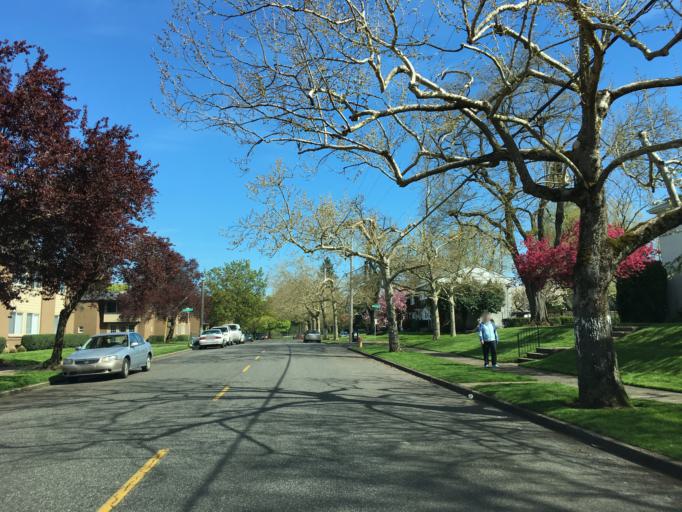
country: US
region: Oregon
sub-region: Multnomah County
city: Lents
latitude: 45.5355
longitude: -122.5943
